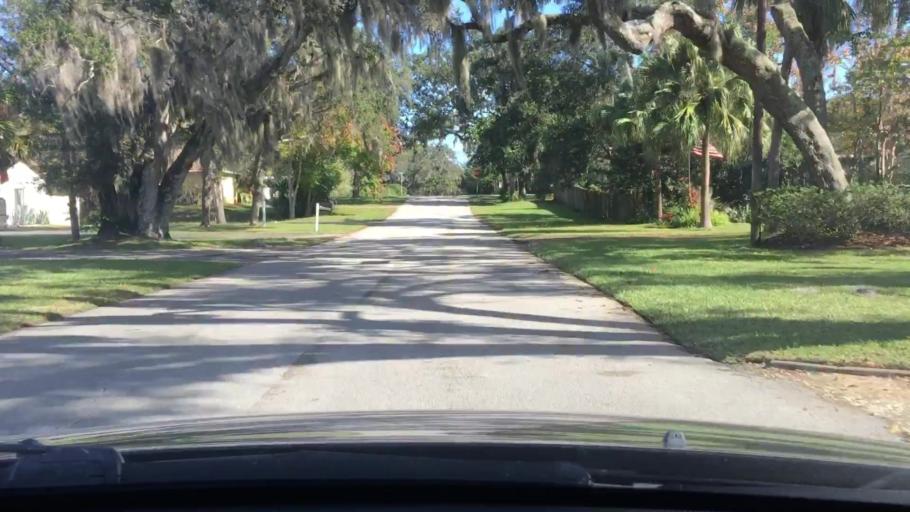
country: US
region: Florida
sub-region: Volusia County
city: Ormond Beach
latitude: 29.2954
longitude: -81.0651
